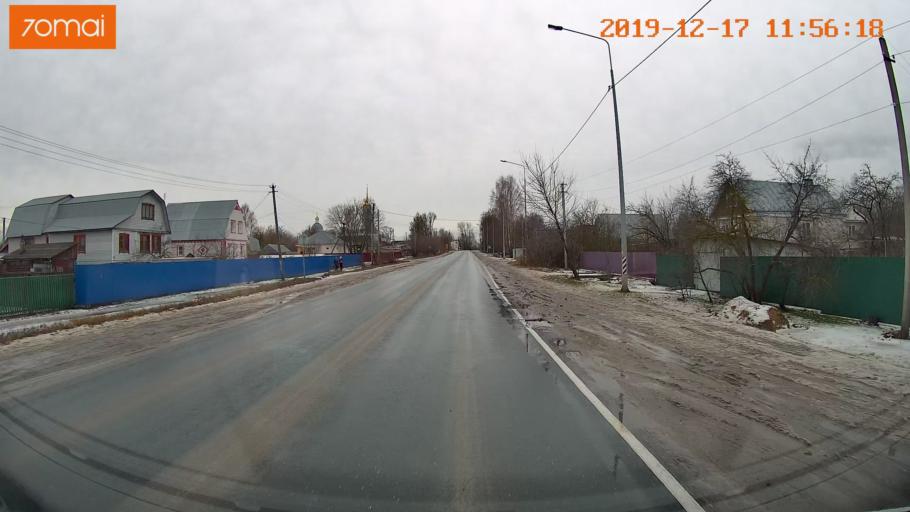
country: RU
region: Rjazan
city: Tuma
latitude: 55.1526
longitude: 40.5550
